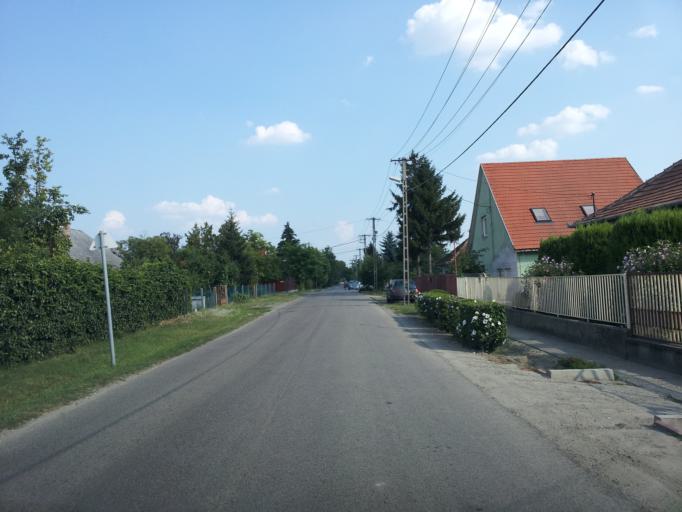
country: HU
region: Pest
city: Szigethalom
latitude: 47.3211
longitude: 18.9961
